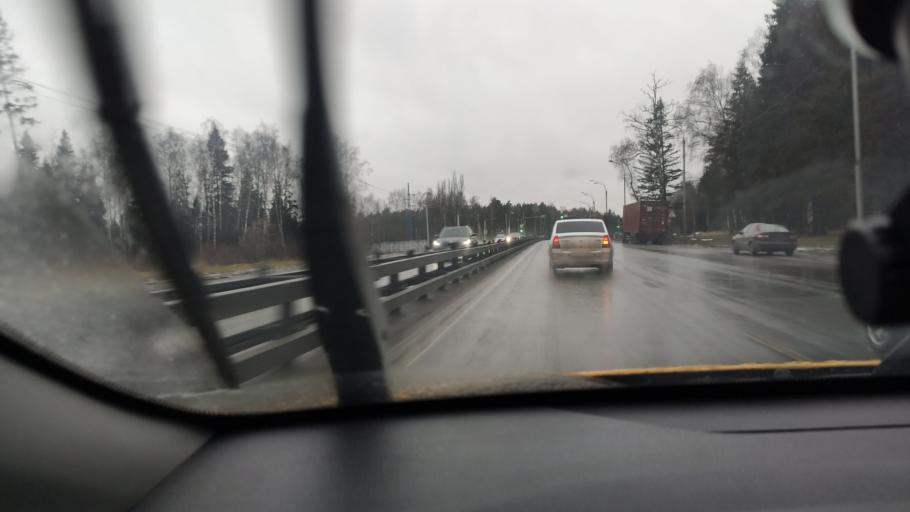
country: RU
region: Moskovskaya
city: Dubrovitsy
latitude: 55.3718
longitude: 37.3884
